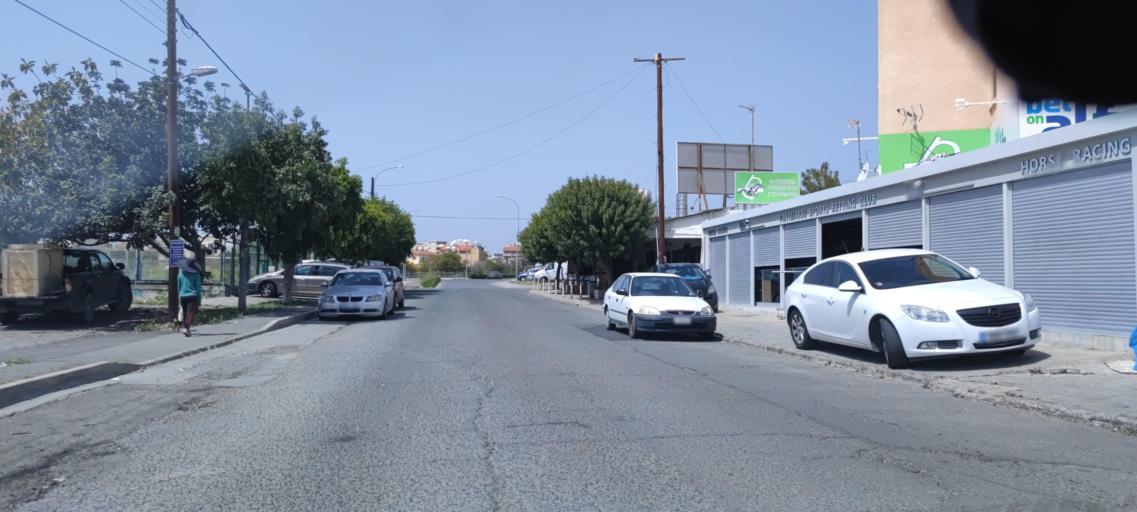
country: CY
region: Limassol
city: Limassol
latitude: 34.6815
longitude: 33.0187
